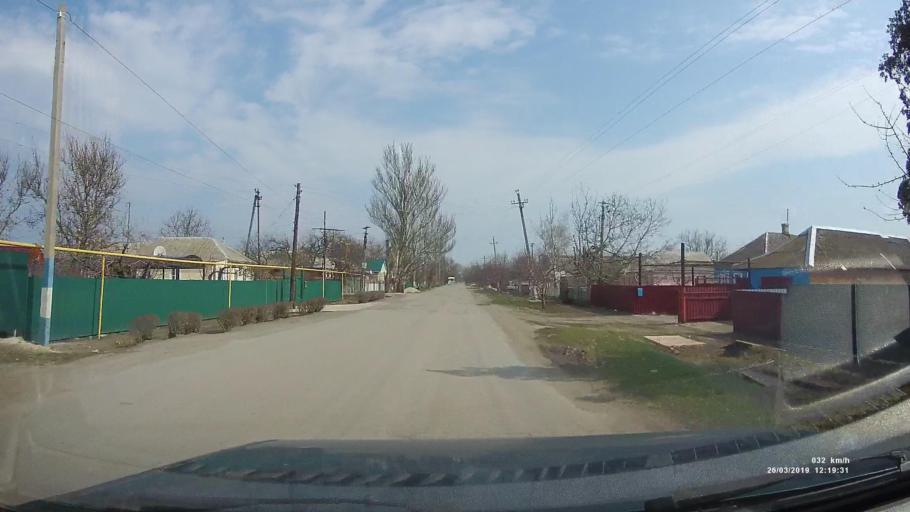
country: RU
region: Rostov
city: Novobessergenovka
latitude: 47.1480
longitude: 38.6483
